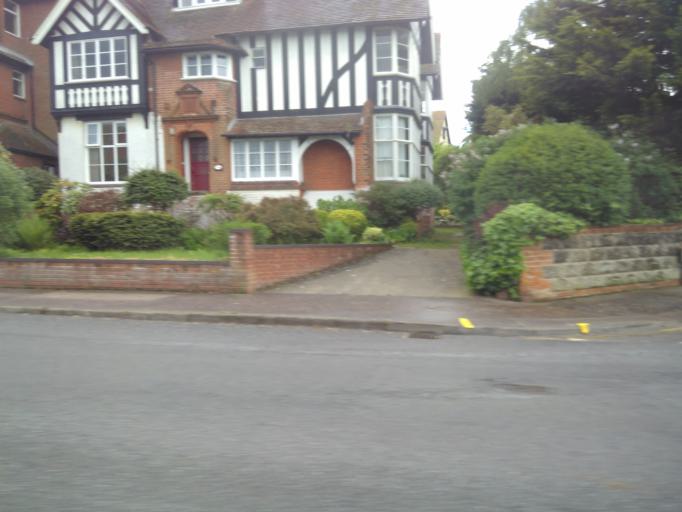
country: GB
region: England
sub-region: Norfolk
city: Sheringham
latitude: 52.9415
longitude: 1.2047
